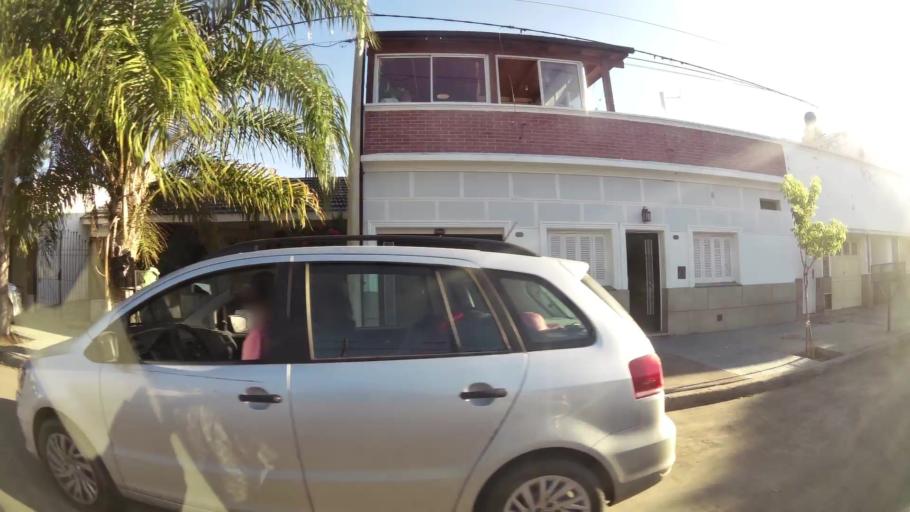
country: AR
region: Cordoba
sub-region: Departamento de Capital
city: Cordoba
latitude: -31.3841
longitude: -64.1832
